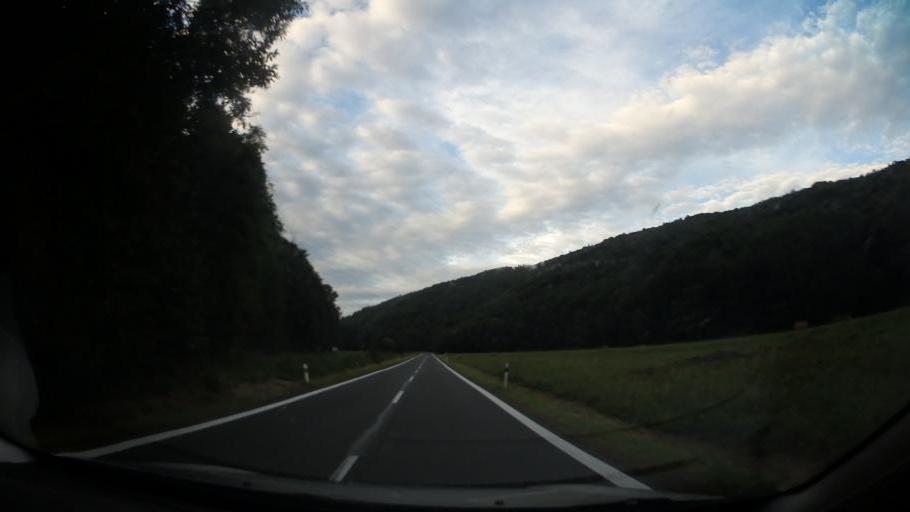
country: CZ
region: Olomoucky
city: Paseka
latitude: 49.8408
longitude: 17.2202
